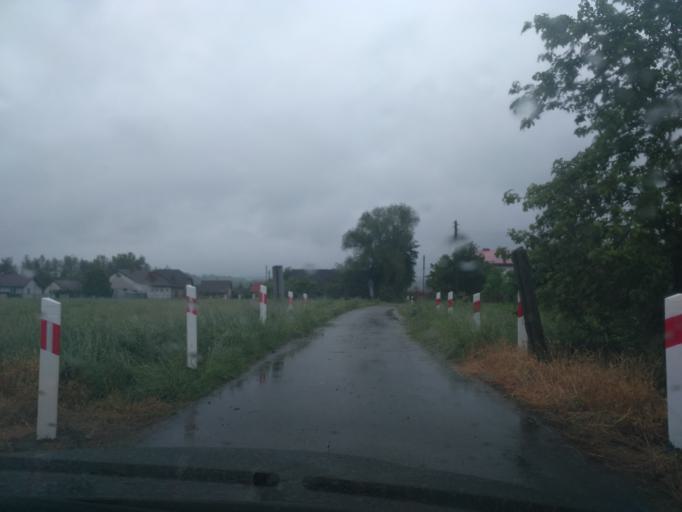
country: PL
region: Subcarpathian Voivodeship
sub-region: Powiat jasielski
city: Jaslo
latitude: 49.7453
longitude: 21.5114
